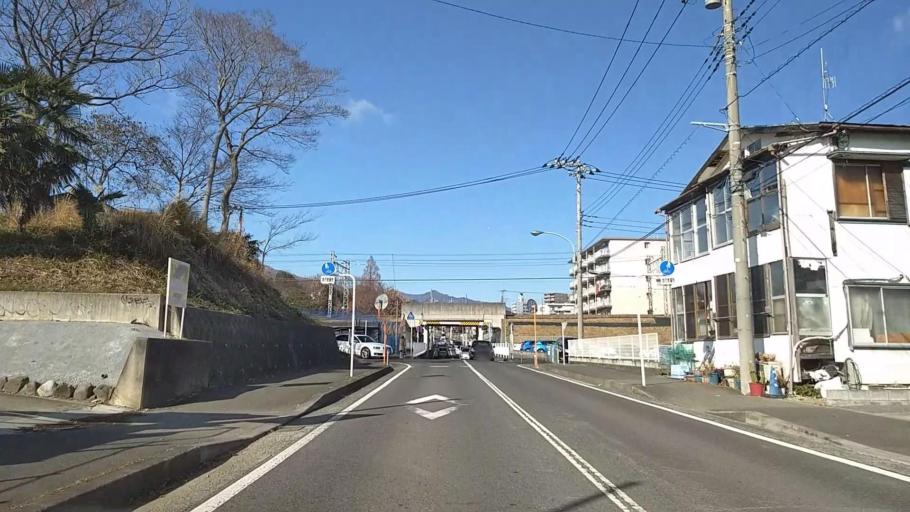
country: JP
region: Kanagawa
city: Isehara
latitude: 35.3932
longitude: 139.3100
